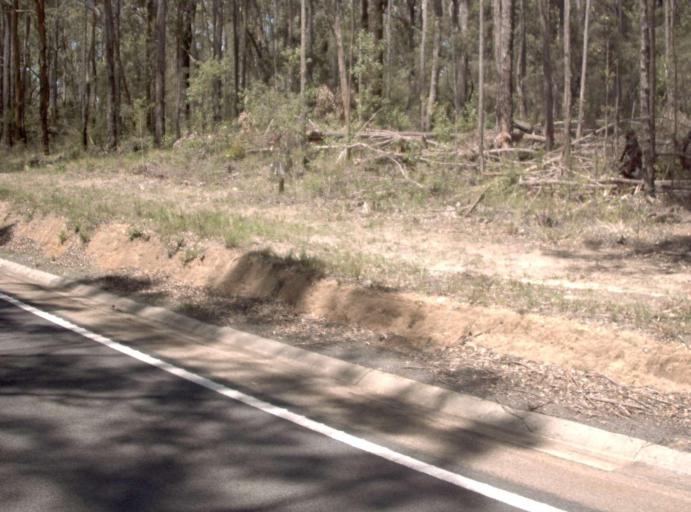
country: AU
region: Victoria
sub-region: East Gippsland
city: Lakes Entrance
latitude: -37.6953
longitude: 148.7436
